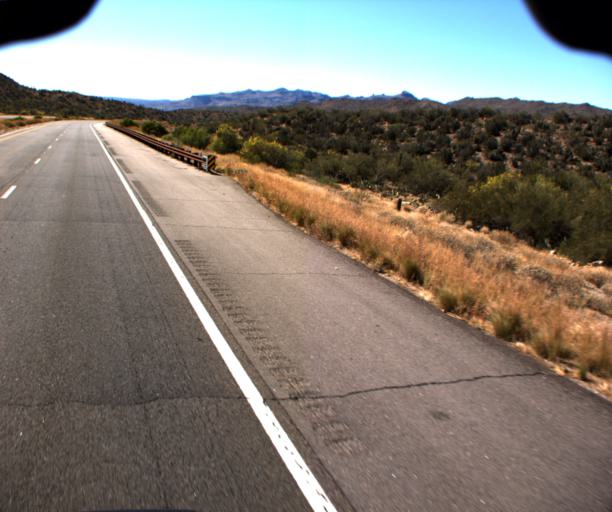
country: US
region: Arizona
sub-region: Yavapai County
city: Bagdad
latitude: 34.4191
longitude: -113.2361
